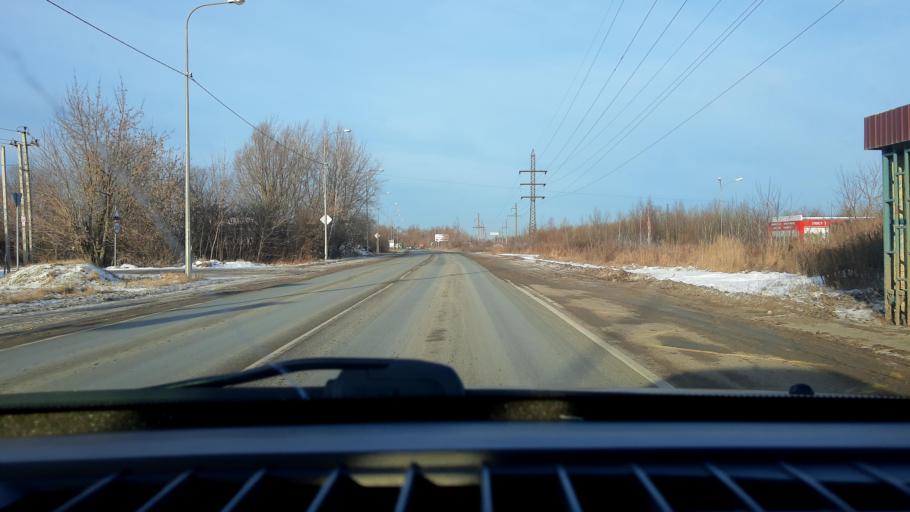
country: RU
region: Nizjnij Novgorod
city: Bor
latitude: 56.3733
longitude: 44.0633
